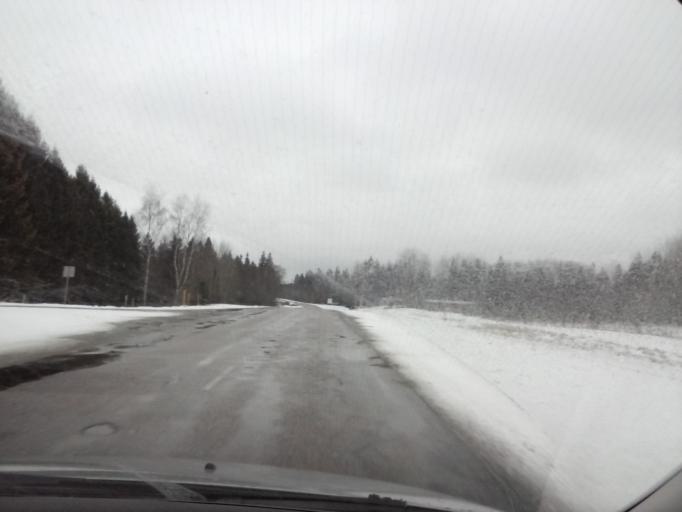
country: LV
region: Valkas Rajons
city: Valka
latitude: 57.7586
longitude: 25.9882
